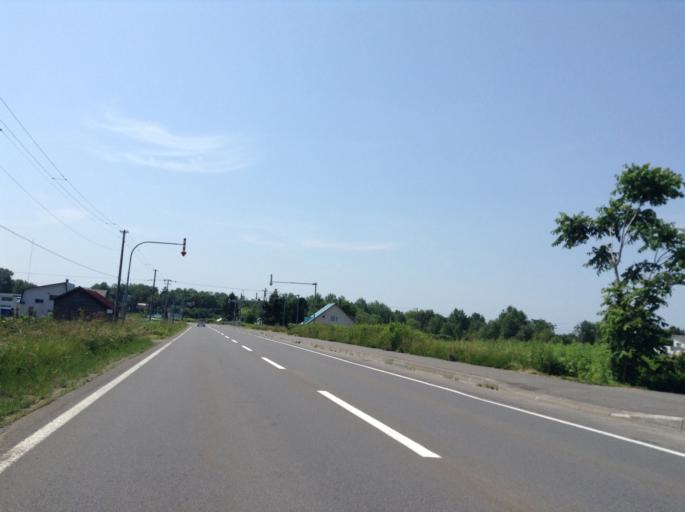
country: JP
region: Hokkaido
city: Nayoro
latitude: 44.3531
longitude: 142.4733
